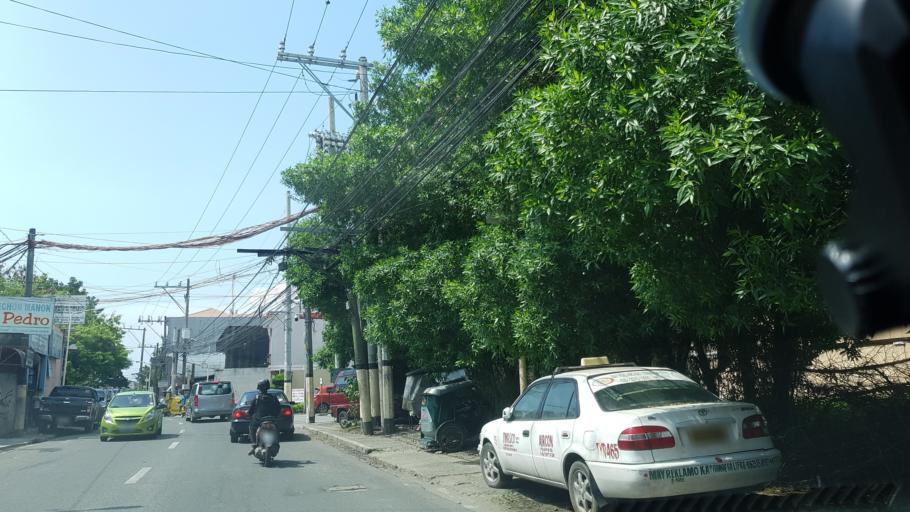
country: PH
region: Calabarzon
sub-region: Province of Rizal
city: Las Pinas
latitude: 14.4687
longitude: 120.9804
